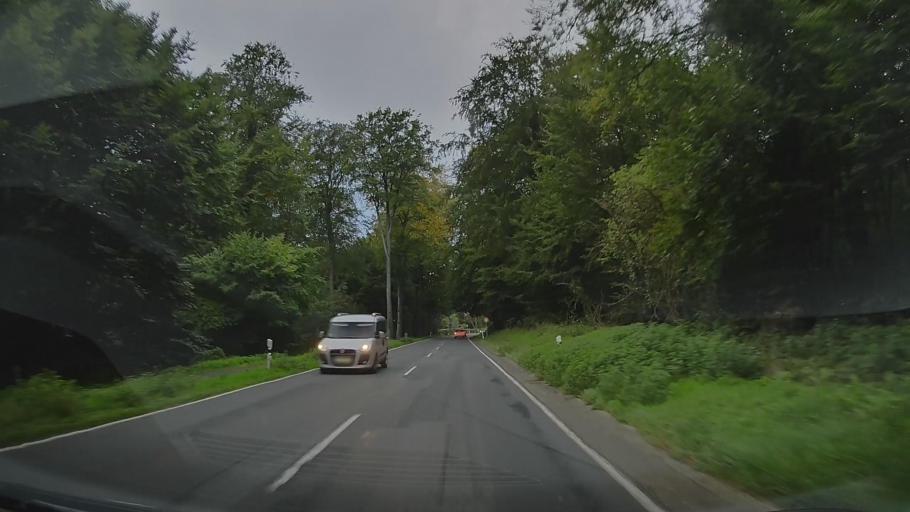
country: DE
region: Lower Saxony
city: Syke
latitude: 52.9118
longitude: 8.8462
